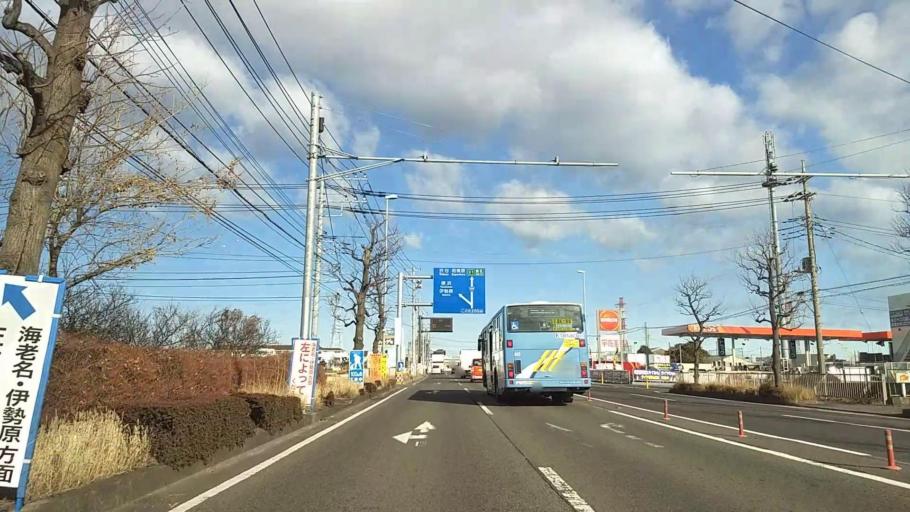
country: JP
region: Kanagawa
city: Atsugi
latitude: 35.3994
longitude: 139.3616
